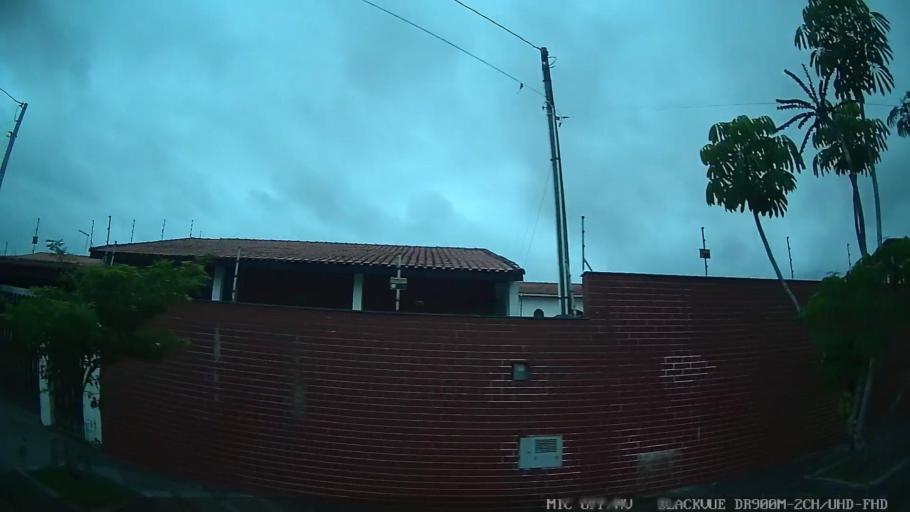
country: BR
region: Sao Paulo
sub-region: Peruibe
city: Peruibe
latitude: -24.3043
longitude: -46.9873
